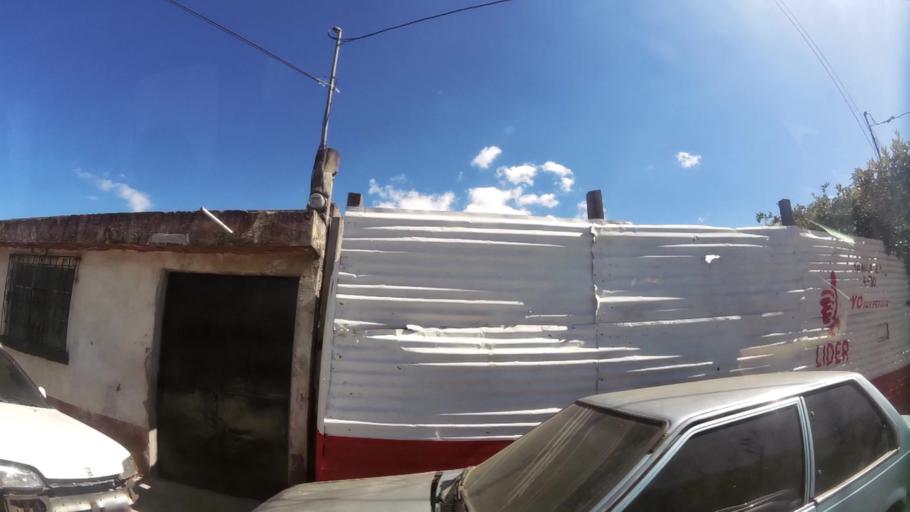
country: GT
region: Guatemala
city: Petapa
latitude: 14.5104
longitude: -90.5675
